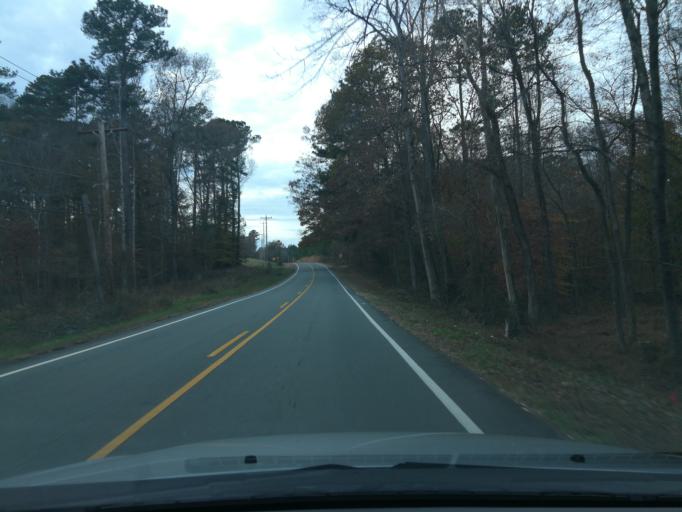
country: US
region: North Carolina
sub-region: Orange County
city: Hillsborough
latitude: 36.0307
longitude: -79.0178
